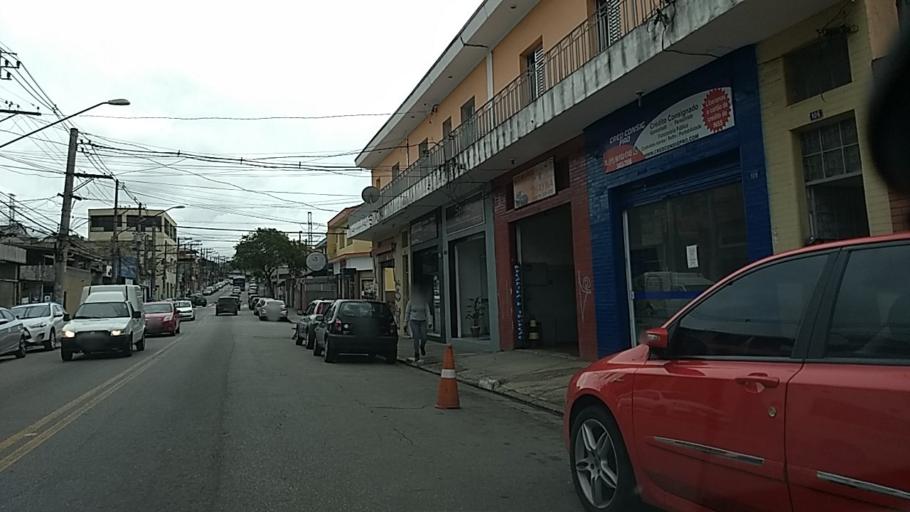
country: BR
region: Sao Paulo
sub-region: Guarulhos
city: Guarulhos
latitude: -23.4885
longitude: -46.5762
